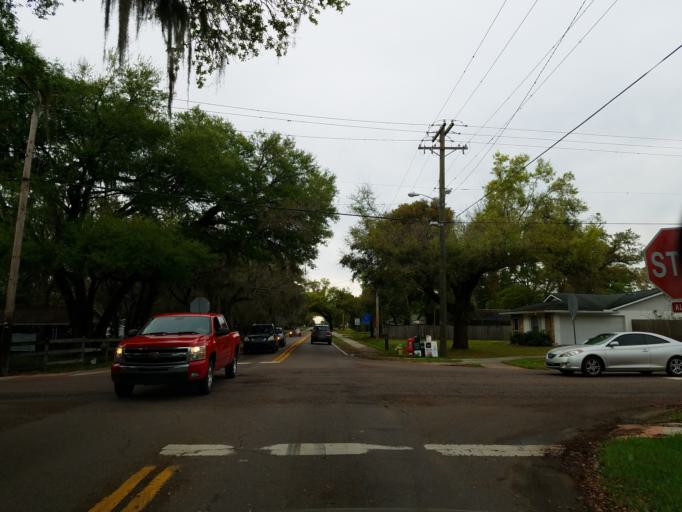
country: US
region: Florida
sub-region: Hillsborough County
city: Valrico
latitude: 27.9232
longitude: -82.2445
